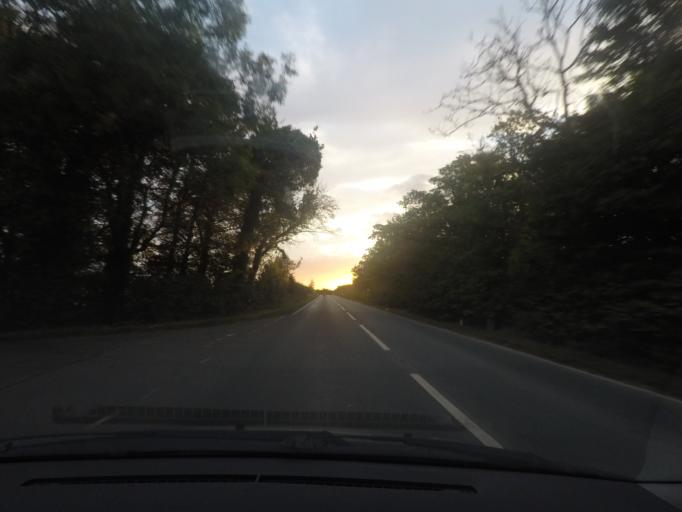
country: GB
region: England
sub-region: North Lincolnshire
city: Croxton
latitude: 53.5854
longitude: -0.3574
